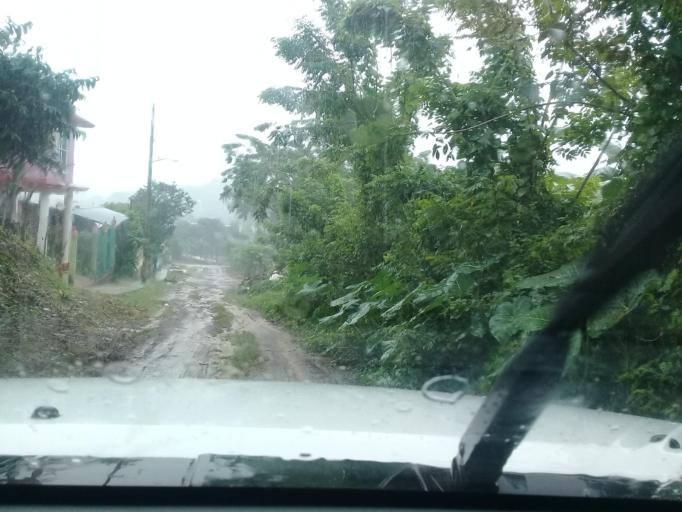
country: MX
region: Veracruz
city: Santiago Tuxtla
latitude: 18.4737
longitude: -95.3044
